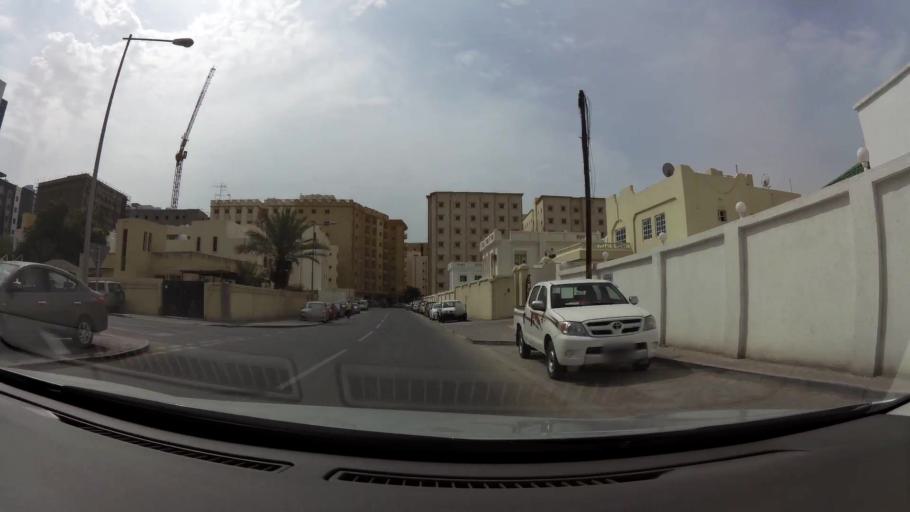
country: QA
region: Baladiyat ad Dawhah
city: Doha
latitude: 25.2852
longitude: 51.5032
